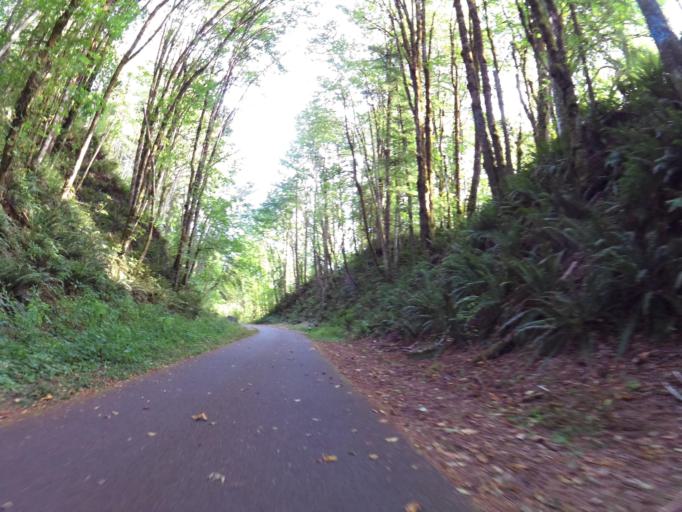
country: US
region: Washington
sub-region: Thurston County
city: Tenino
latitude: 46.9334
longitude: -122.8242
